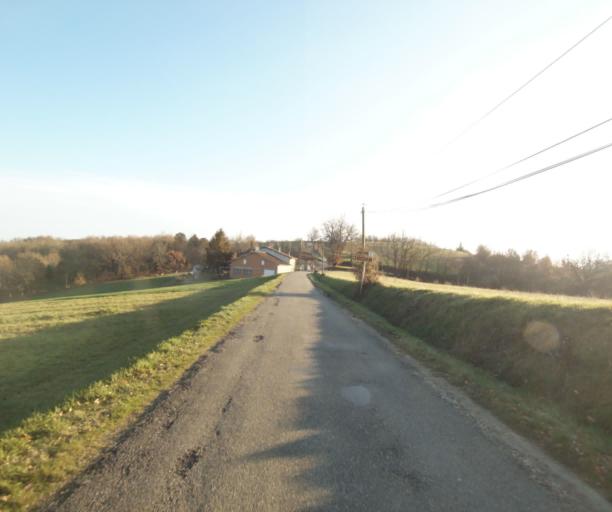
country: FR
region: Midi-Pyrenees
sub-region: Departement du Tarn-et-Garonne
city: Moissac
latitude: 44.1321
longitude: 1.1381
